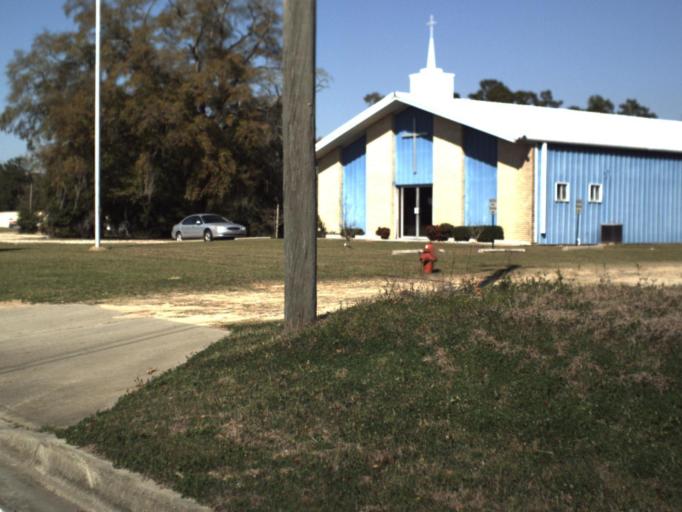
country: US
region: Florida
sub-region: Jackson County
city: Marianna
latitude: 30.7461
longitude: -85.1870
